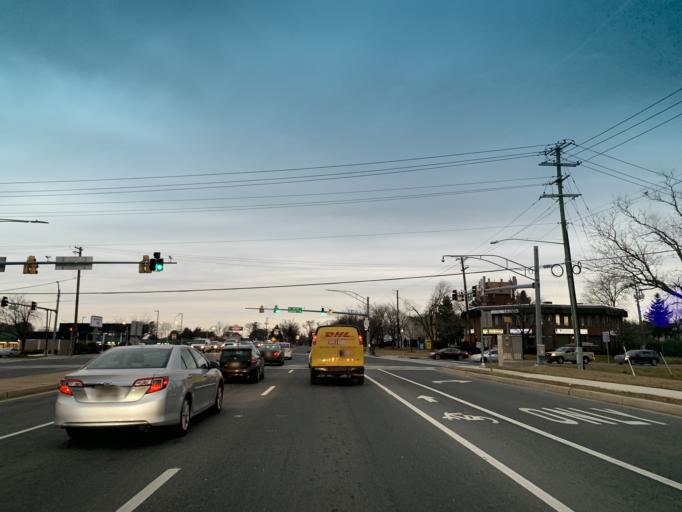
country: US
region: Maryland
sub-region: Montgomery County
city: Layhill
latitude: 39.0901
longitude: -77.0446
